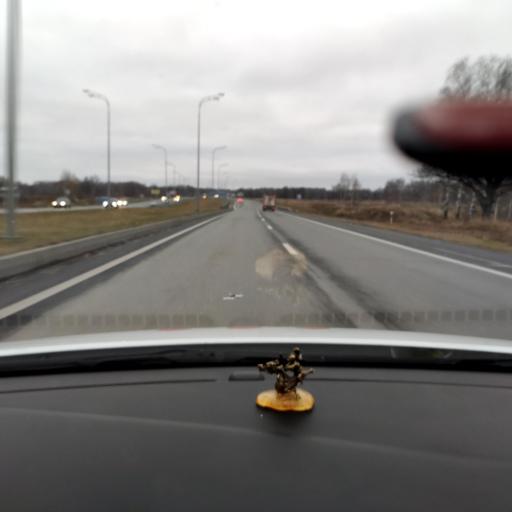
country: RU
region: Tatarstan
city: Osinovo
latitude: 55.8639
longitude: 48.7930
